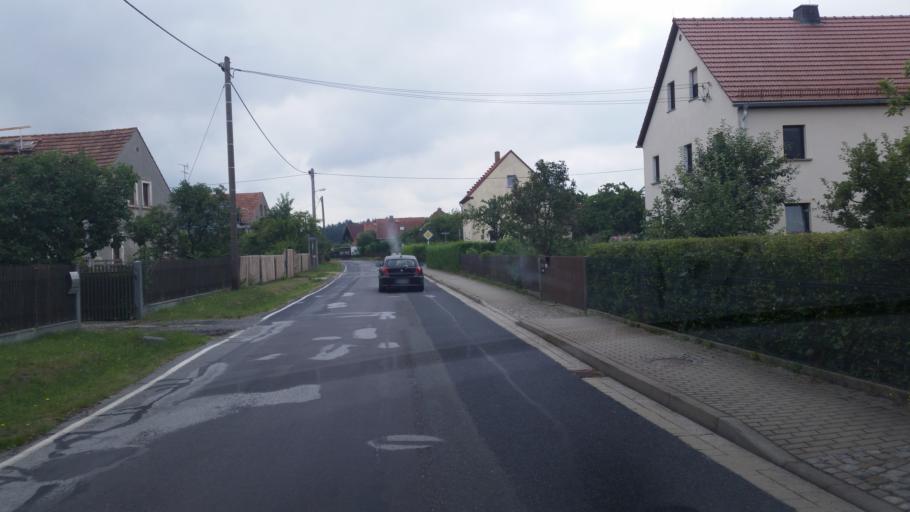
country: DE
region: Saxony
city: Laussnitz
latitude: 51.2448
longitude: 13.8826
